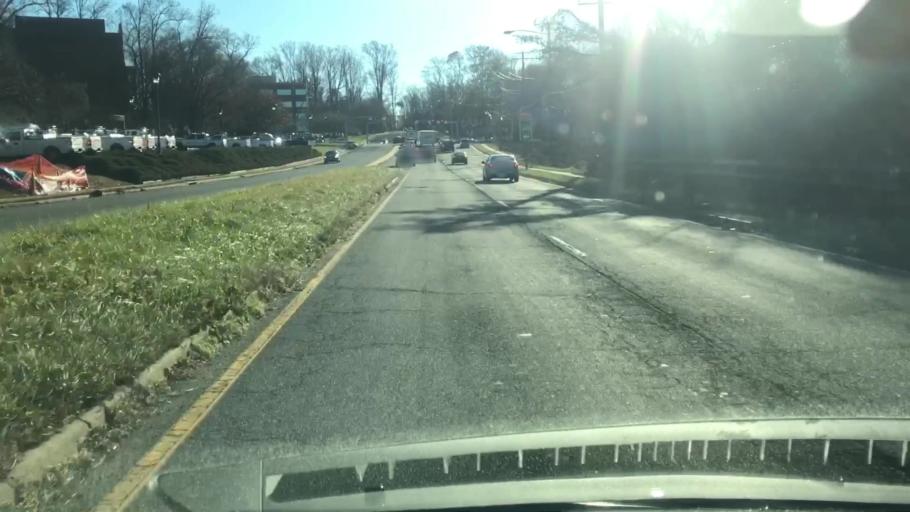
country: US
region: Virginia
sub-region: Fairfax County
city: Merrifield
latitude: 38.8673
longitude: -77.2393
